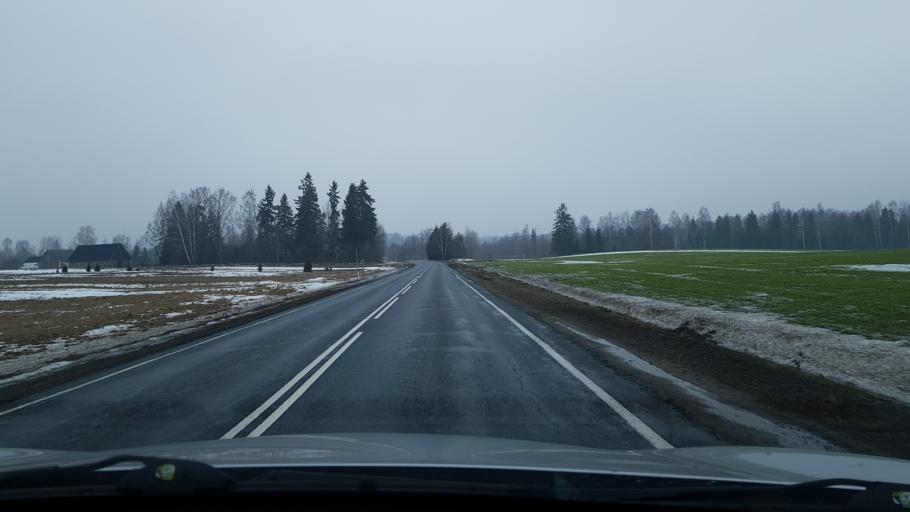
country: EE
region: Valgamaa
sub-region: Torva linn
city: Torva
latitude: 58.1401
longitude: 25.9874
